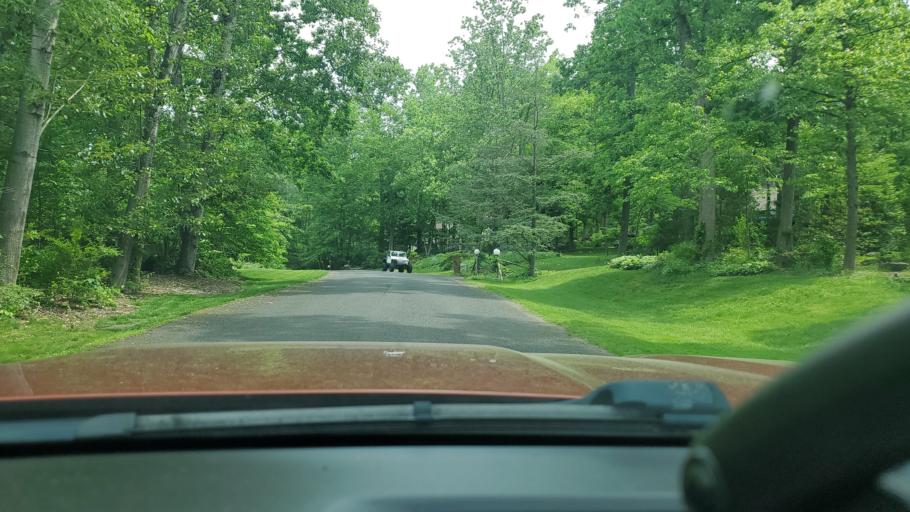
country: US
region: Pennsylvania
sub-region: Montgomery County
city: Woxall
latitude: 40.3163
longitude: -75.4903
